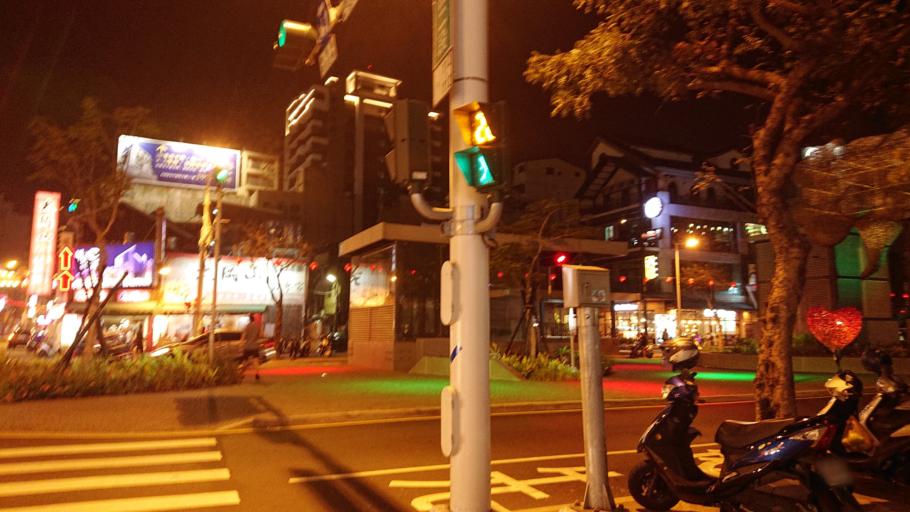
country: TW
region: Taiwan
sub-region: Tainan
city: Tainan
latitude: 22.9954
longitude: 120.1969
